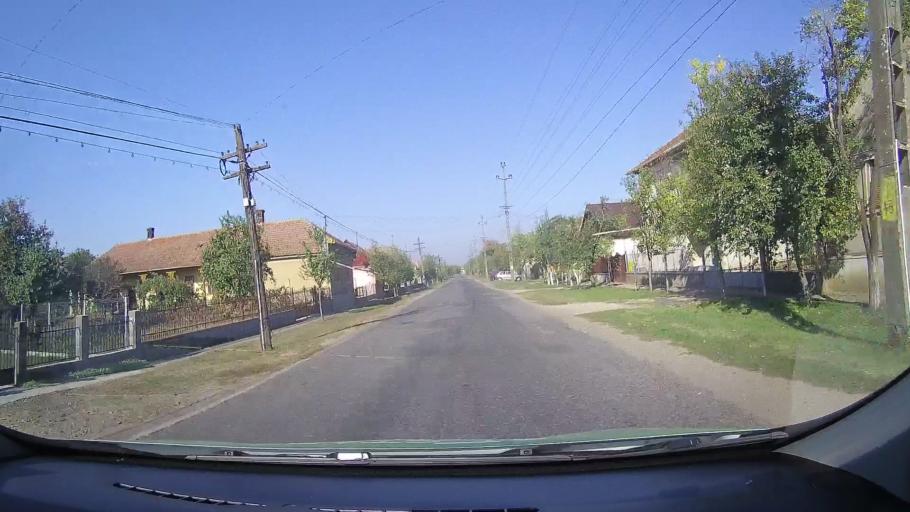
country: RO
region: Satu Mare
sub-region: Comuna Petresti
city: Petresti
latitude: 47.6067
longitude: 22.3604
